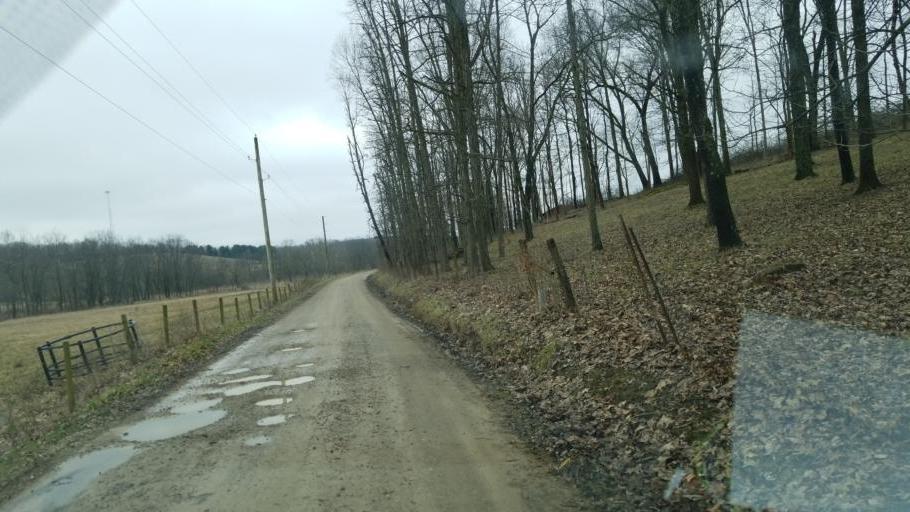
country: US
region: Ohio
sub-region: Knox County
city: Gambier
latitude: 40.4649
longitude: -82.4107
